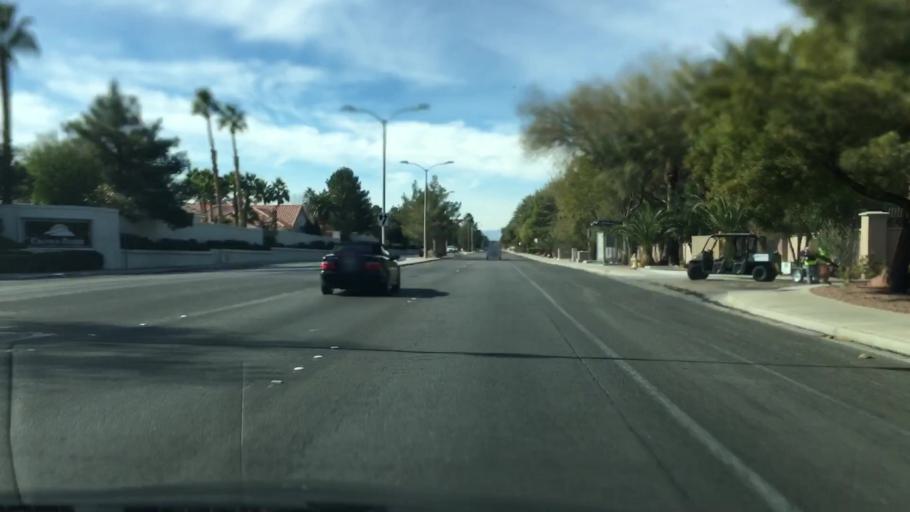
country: US
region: Nevada
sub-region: Clark County
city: Whitney
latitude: 36.0564
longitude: -115.0734
